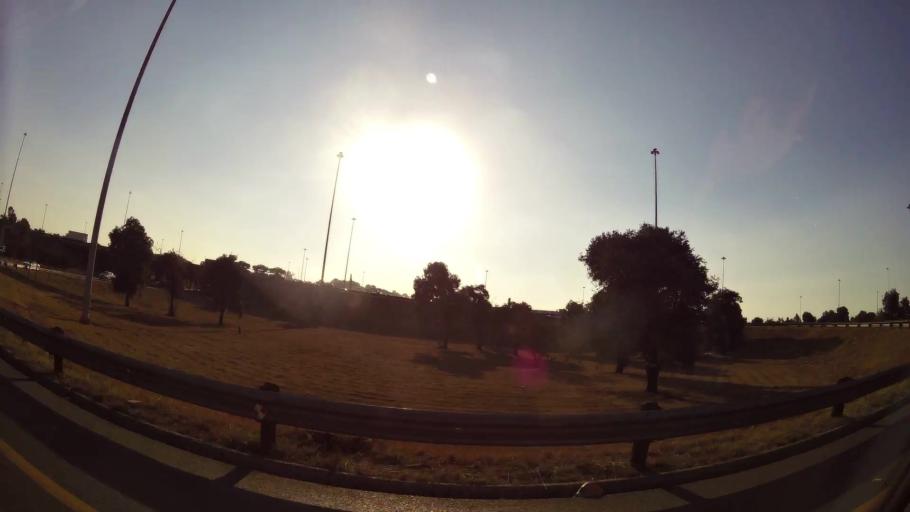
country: ZA
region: Gauteng
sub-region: Ekurhuleni Metropolitan Municipality
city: Germiston
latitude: -26.2126
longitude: 28.1361
